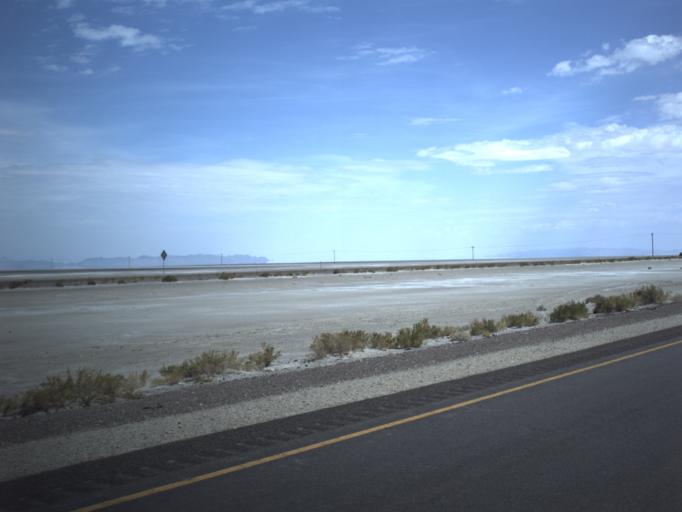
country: US
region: Utah
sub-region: Tooele County
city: Wendover
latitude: 40.7368
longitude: -113.7712
